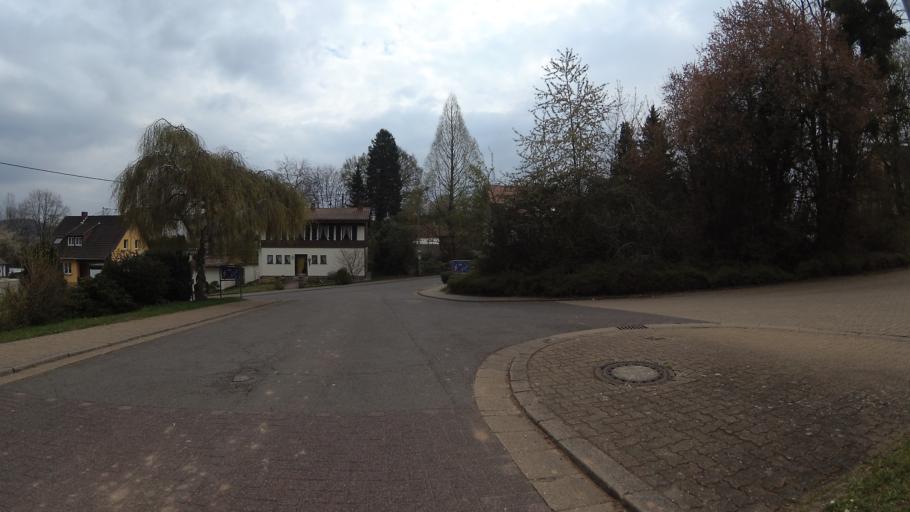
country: DE
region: Saarland
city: Merzig
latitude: 49.4378
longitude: 6.6132
